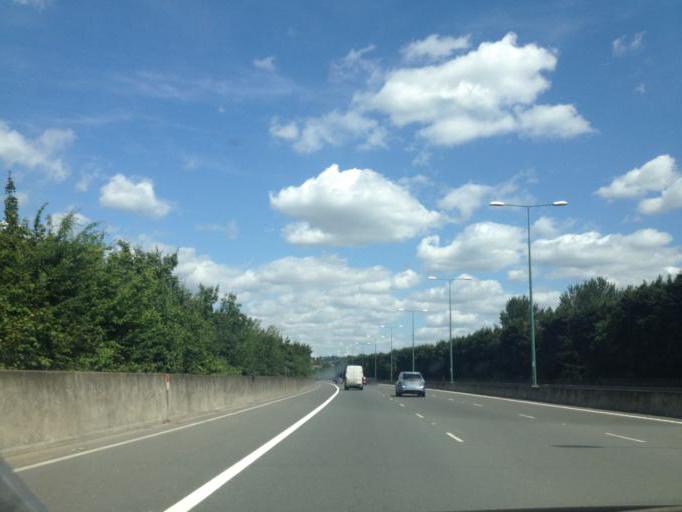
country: GB
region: England
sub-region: Greater London
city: Hendon
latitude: 51.5942
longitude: -0.2358
